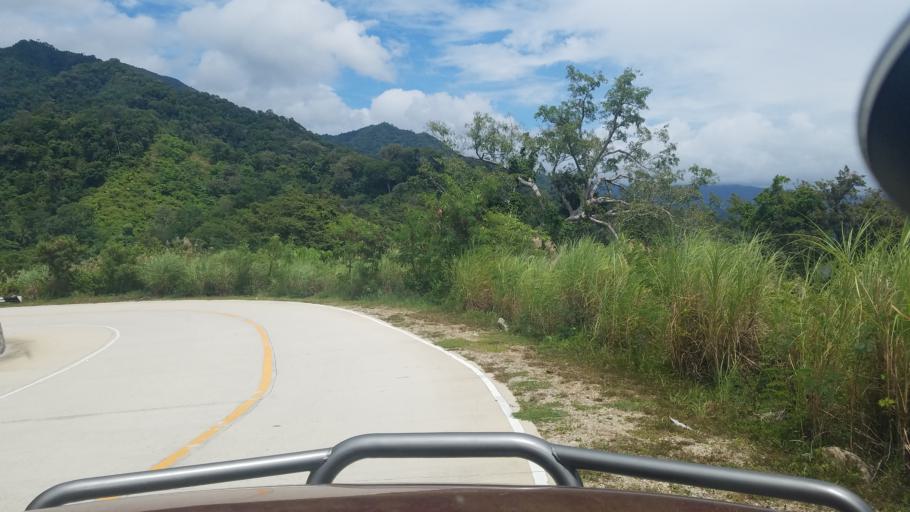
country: PH
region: Cagayan Valley
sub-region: Province of Quirino
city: Nagtipunan
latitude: 16.0517
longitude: 121.7239
